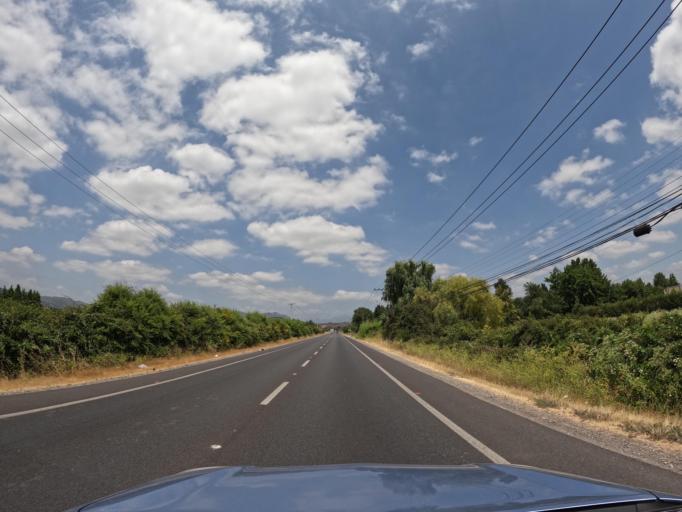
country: CL
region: Maule
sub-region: Provincia de Curico
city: Curico
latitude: -35.0229
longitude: -71.2031
